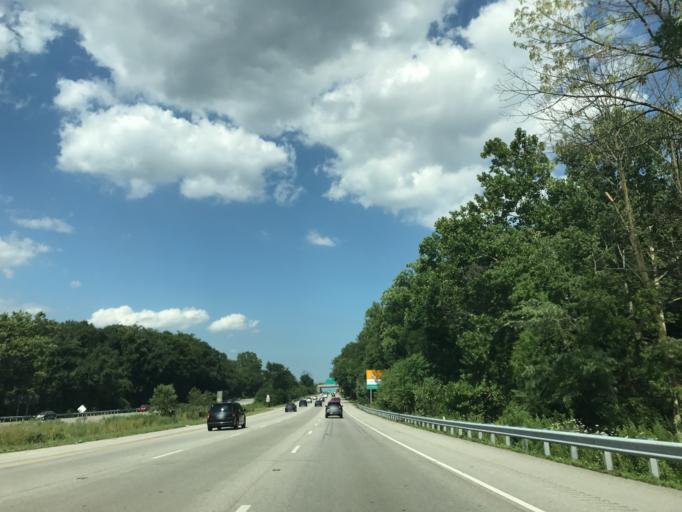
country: US
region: Maryland
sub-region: Anne Arundel County
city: Linthicum
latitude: 39.2156
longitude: -76.6690
